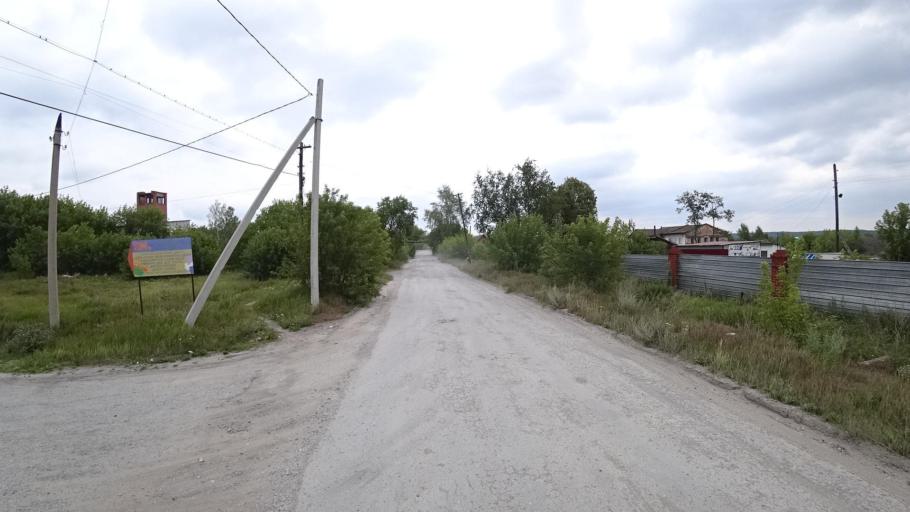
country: RU
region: Sverdlovsk
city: Kamyshlov
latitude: 56.8331
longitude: 62.7208
